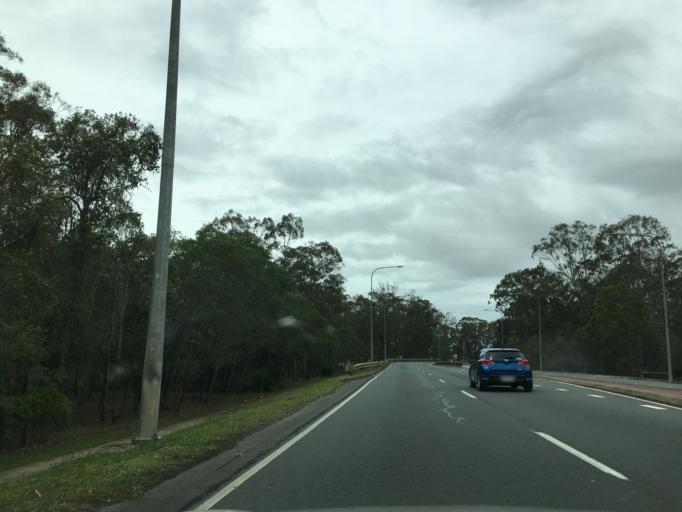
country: AU
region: Queensland
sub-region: Logan
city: Slacks Creek
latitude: -27.6522
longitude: 153.1454
